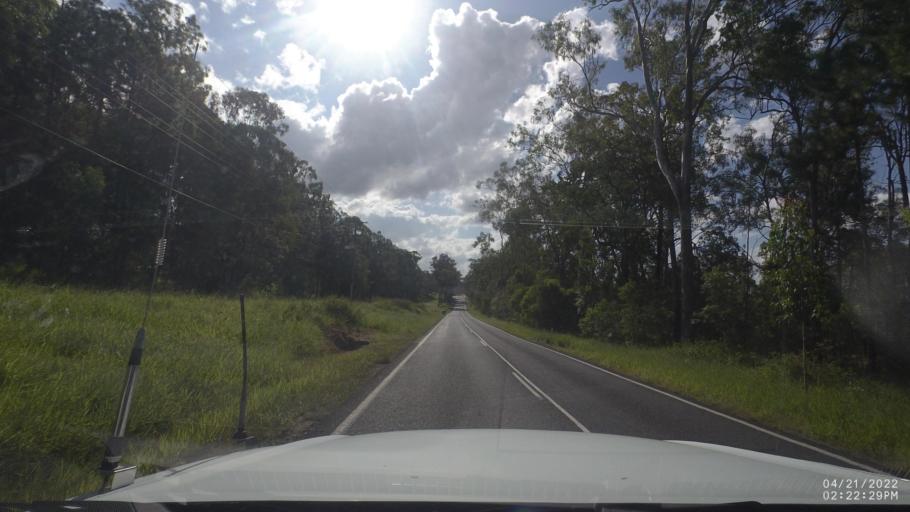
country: AU
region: Queensland
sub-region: Logan
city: Chambers Flat
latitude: -27.8251
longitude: 153.1034
